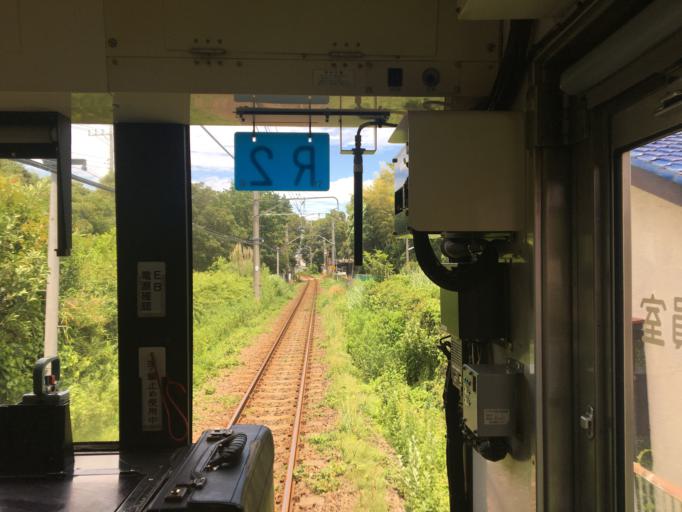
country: JP
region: Kanagawa
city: Atsugi
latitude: 35.4263
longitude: 139.3788
